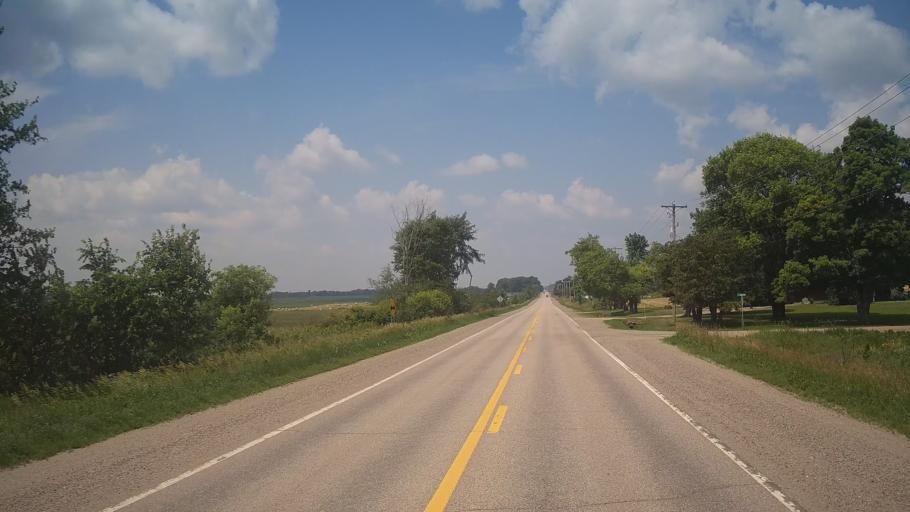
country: CA
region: Quebec
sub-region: Outaouais
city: Shawville
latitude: 45.5882
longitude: -76.4631
